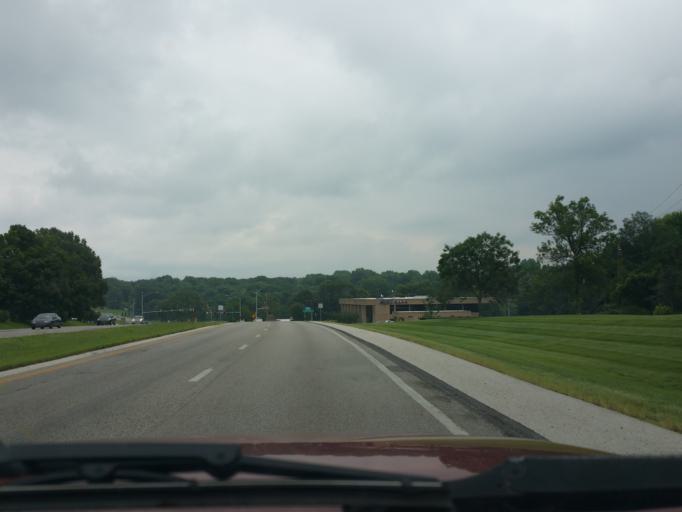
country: US
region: Kansas
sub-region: Johnson County
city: Mission
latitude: 39.0151
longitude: -94.6521
